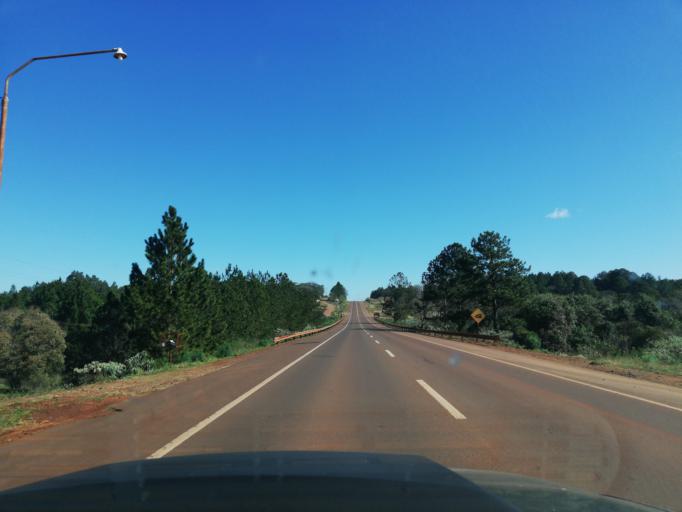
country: AR
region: Misiones
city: Aristobulo del Valle
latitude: -27.0915
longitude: -54.8647
